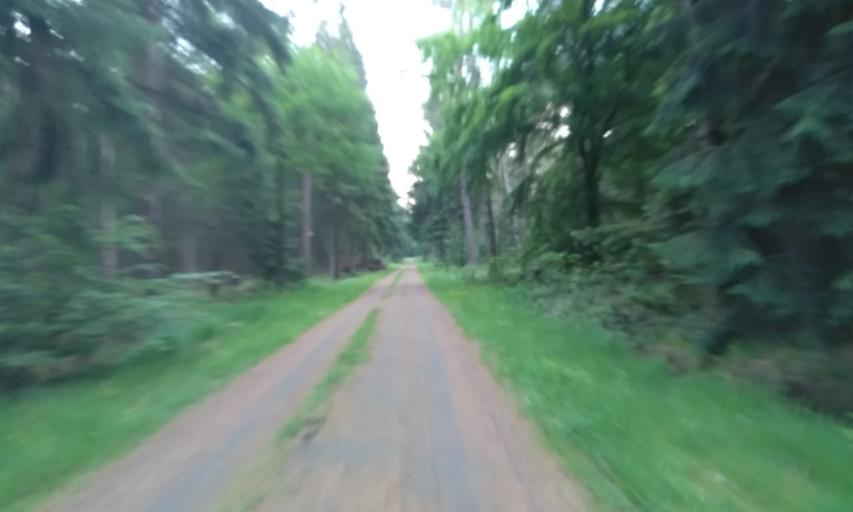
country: DE
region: Lower Saxony
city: Agathenburg
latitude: 53.5280
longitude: 9.5025
